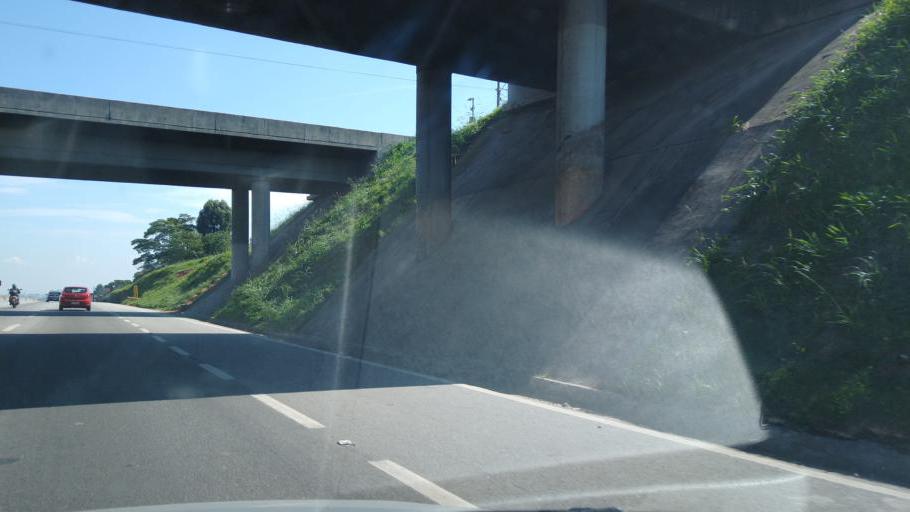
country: BR
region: Sao Paulo
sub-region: Guarulhos
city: Guarulhos
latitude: -23.4548
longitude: -46.4739
